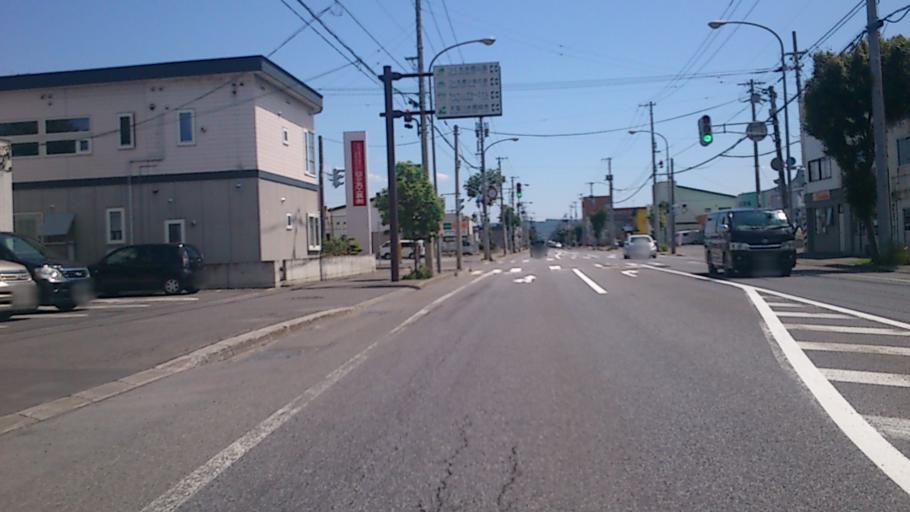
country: JP
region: Hokkaido
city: Nayoro
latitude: 44.1839
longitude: 142.3897
